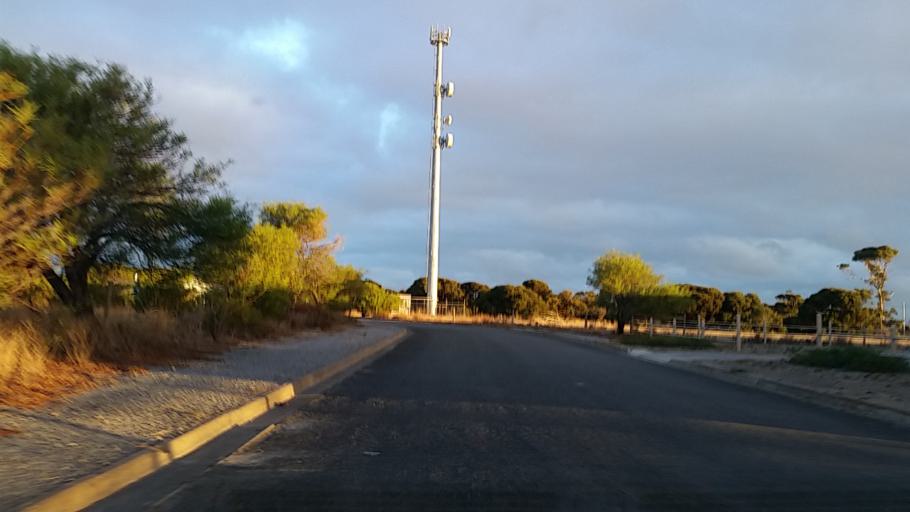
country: AU
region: South Australia
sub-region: Yankalilla
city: Normanville
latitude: -35.6048
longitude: 138.1083
